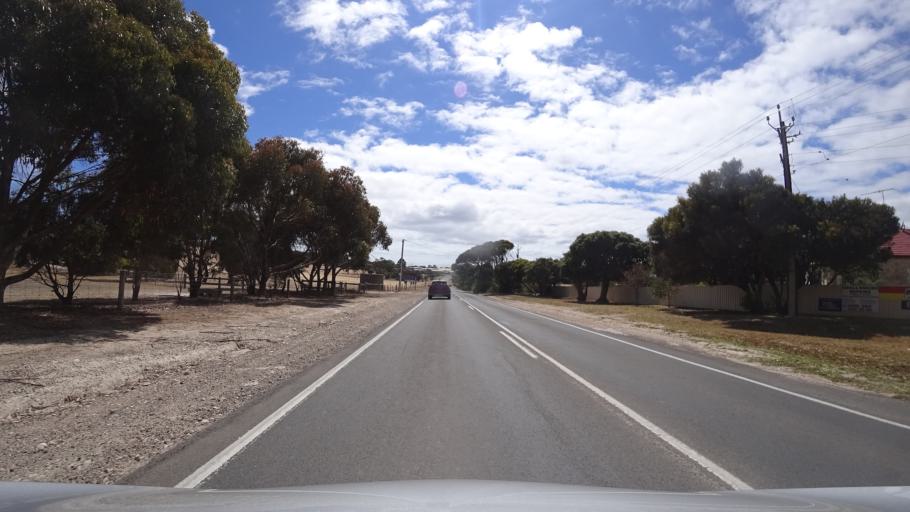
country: AU
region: South Australia
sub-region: Kangaroo Island
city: Kingscote
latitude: -35.6540
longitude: 137.6230
